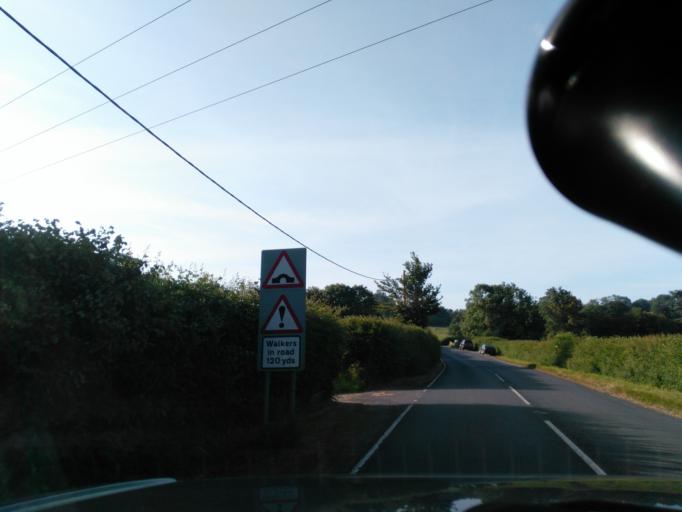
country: GB
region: England
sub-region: Wiltshire
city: Seend
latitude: 51.3533
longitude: -2.0925
